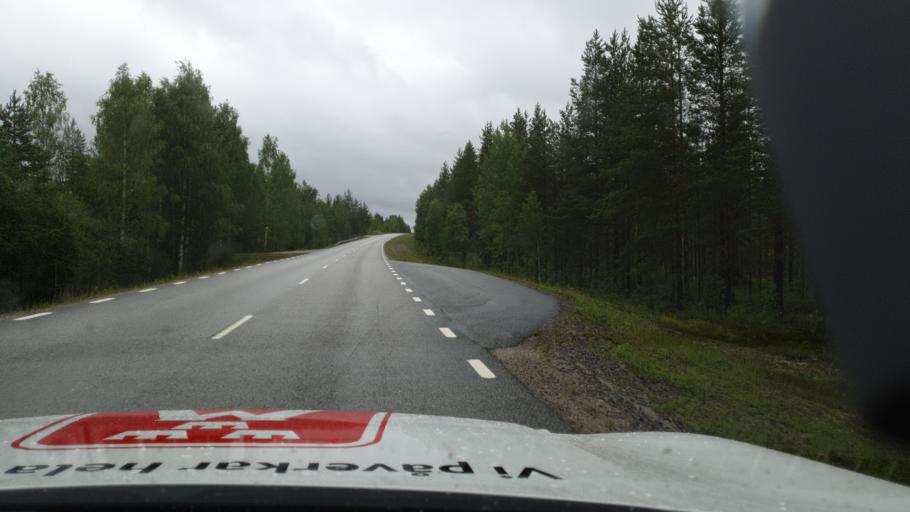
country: SE
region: Vaesterbotten
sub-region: Vindelns Kommun
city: Vindeln
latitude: 64.3293
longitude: 19.5185
